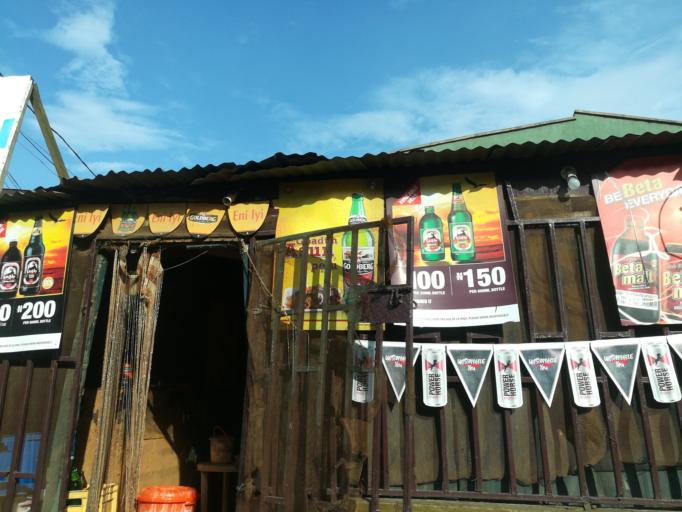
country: NG
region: Lagos
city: Ojota
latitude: 6.6026
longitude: 3.4189
